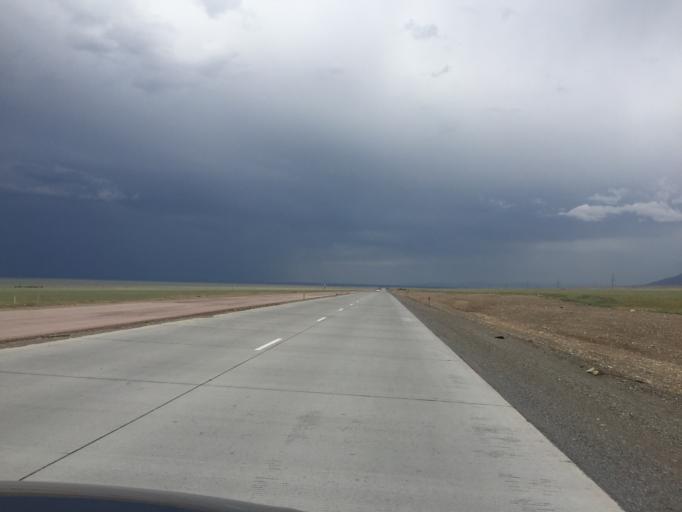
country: KG
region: Chuy
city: Ivanovka
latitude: 43.3817
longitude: 75.1957
